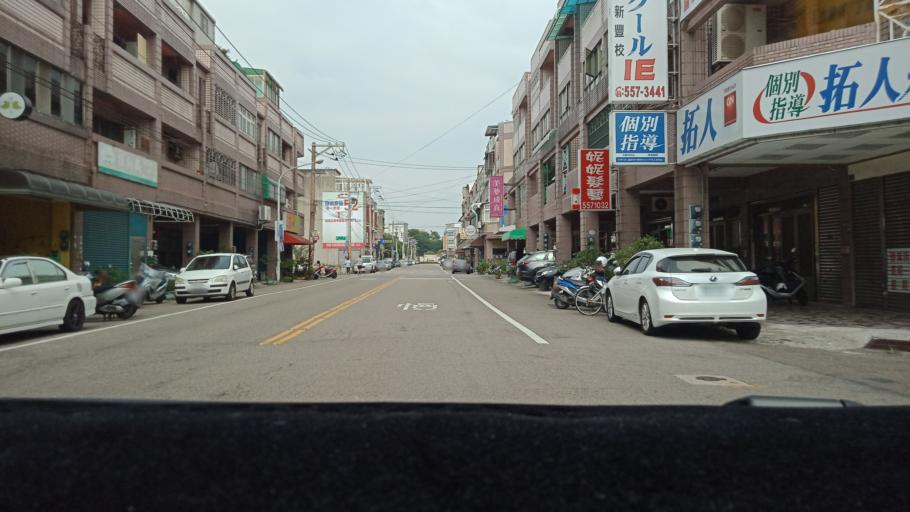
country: TW
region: Taiwan
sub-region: Hsinchu
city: Zhubei
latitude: 24.8769
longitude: 120.9971
